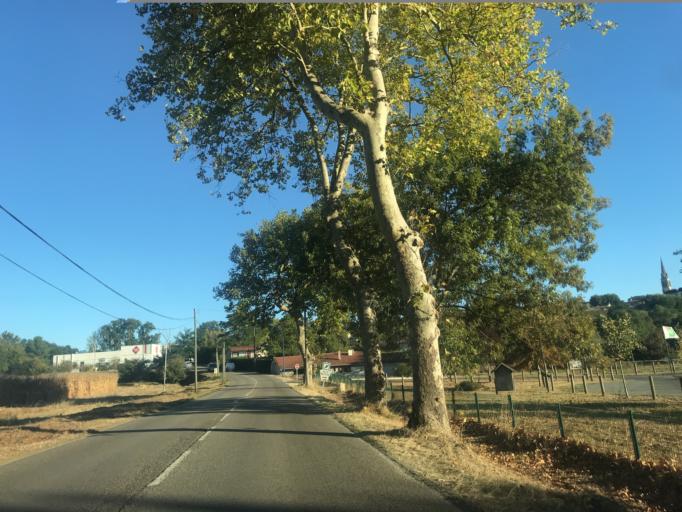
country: FR
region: Poitou-Charentes
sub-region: Departement de la Charente-Maritime
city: Saint-Aigulin
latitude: 45.1574
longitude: 0.0040
